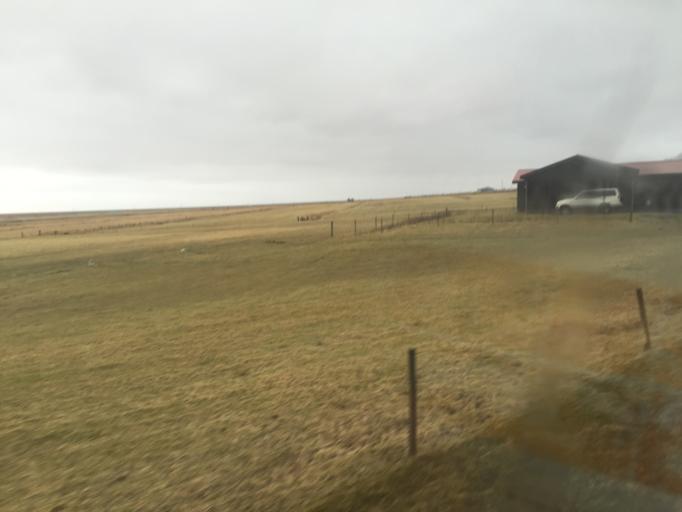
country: IS
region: East
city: Hoefn
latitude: 63.9027
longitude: -16.7016
